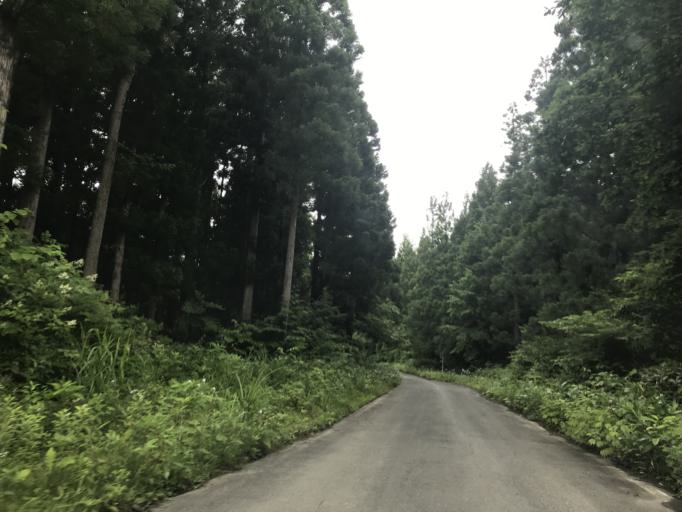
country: JP
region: Iwate
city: Ichinoseki
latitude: 38.9582
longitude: 140.8903
